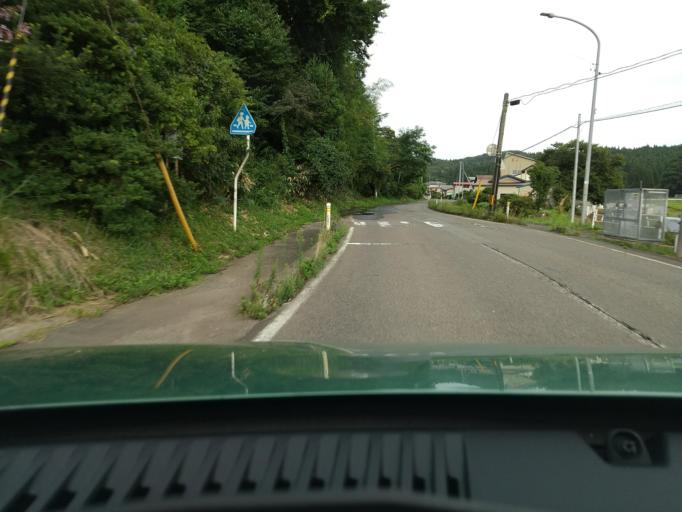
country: JP
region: Akita
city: Akita
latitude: 39.7815
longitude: 140.1322
